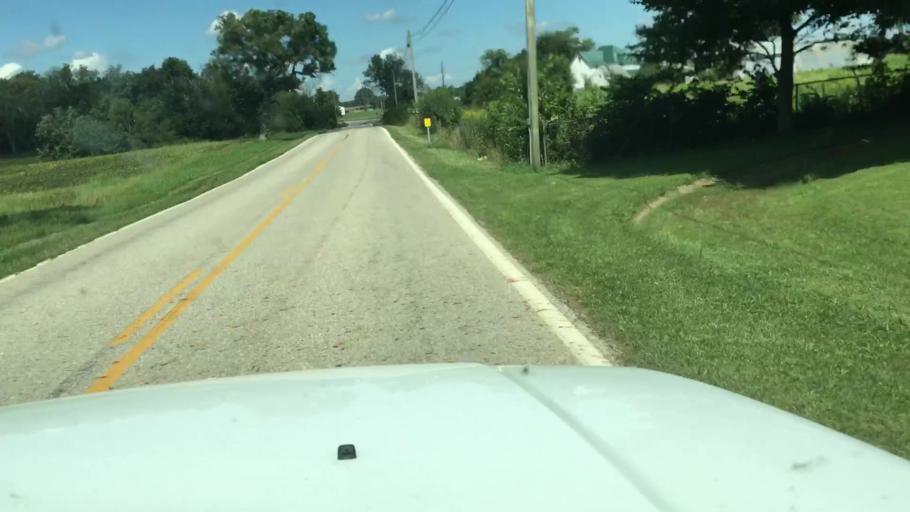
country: US
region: Ohio
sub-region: Madison County
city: Mount Sterling
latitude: 39.7092
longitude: -83.2441
